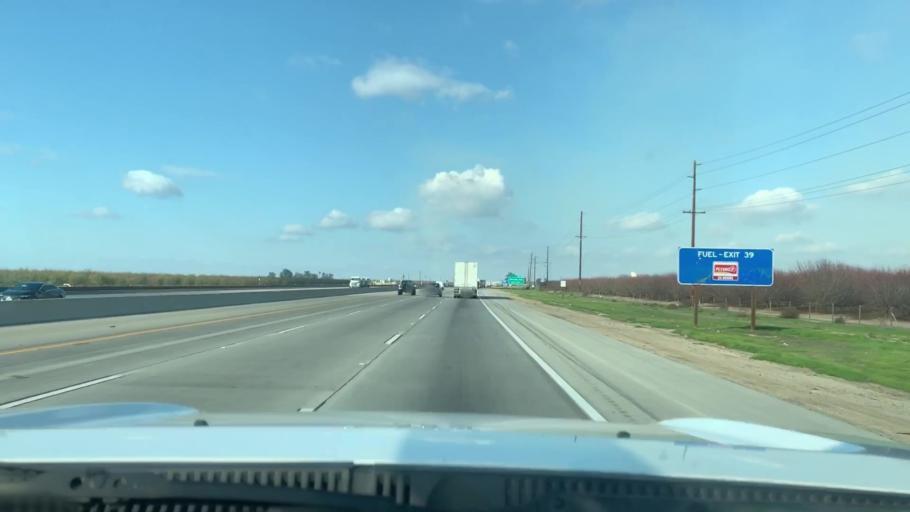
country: US
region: California
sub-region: Kern County
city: Shafter
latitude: 35.5177
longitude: -119.1832
